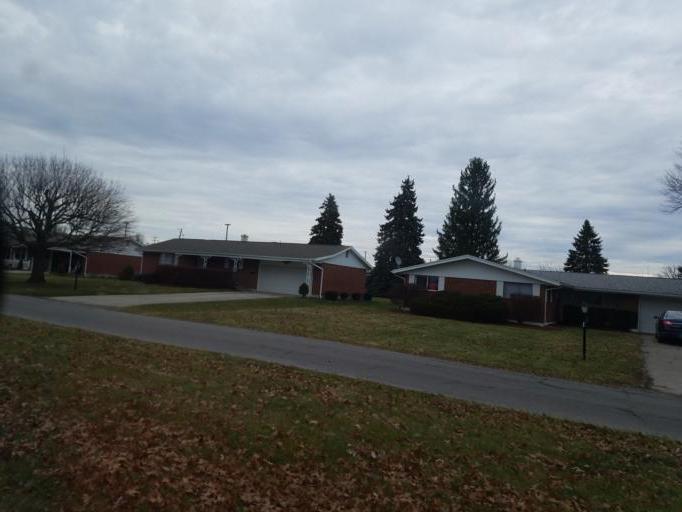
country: US
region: Ohio
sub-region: Marion County
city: Marion
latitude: 40.5788
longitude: -83.0826
